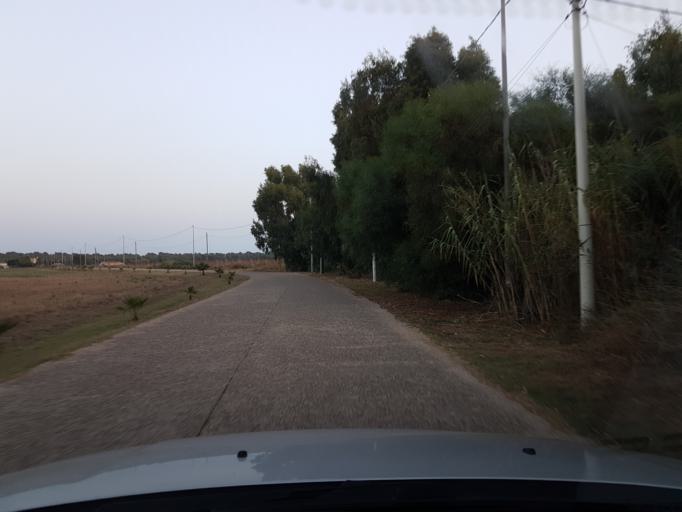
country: IT
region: Sardinia
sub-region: Provincia di Oristano
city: Cabras
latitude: 39.9175
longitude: 8.5080
